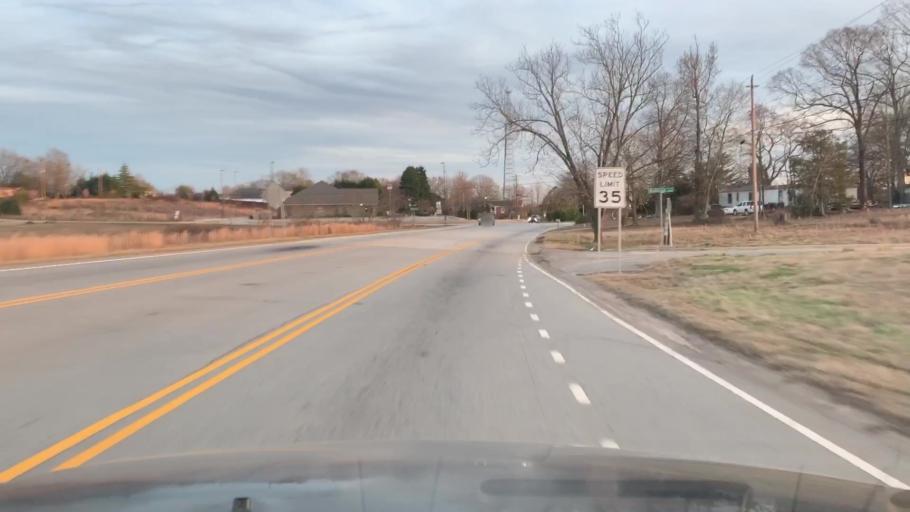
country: US
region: South Carolina
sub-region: Anderson County
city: Powdersville
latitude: 34.7734
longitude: -82.4611
